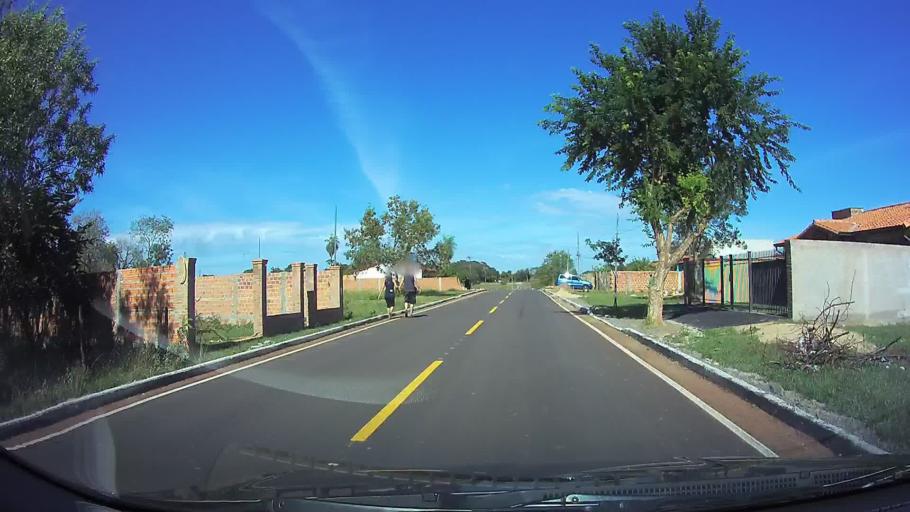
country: PY
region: Central
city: Limpio
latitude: -25.2567
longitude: -57.4647
